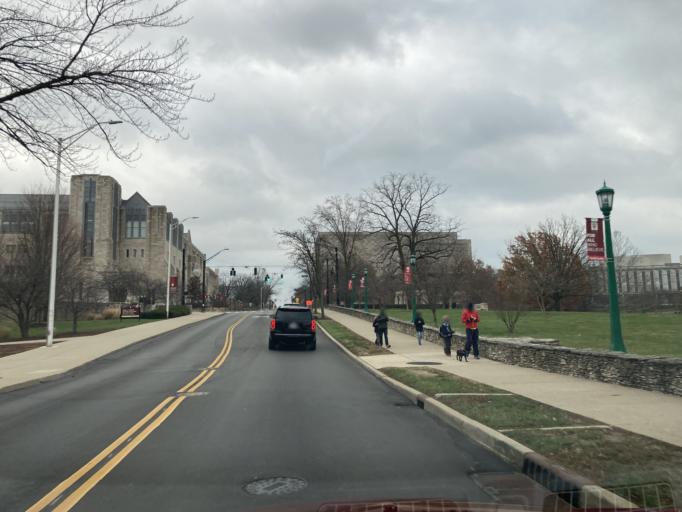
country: US
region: Indiana
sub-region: Monroe County
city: Bloomington
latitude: 39.1716
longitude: -86.5201
